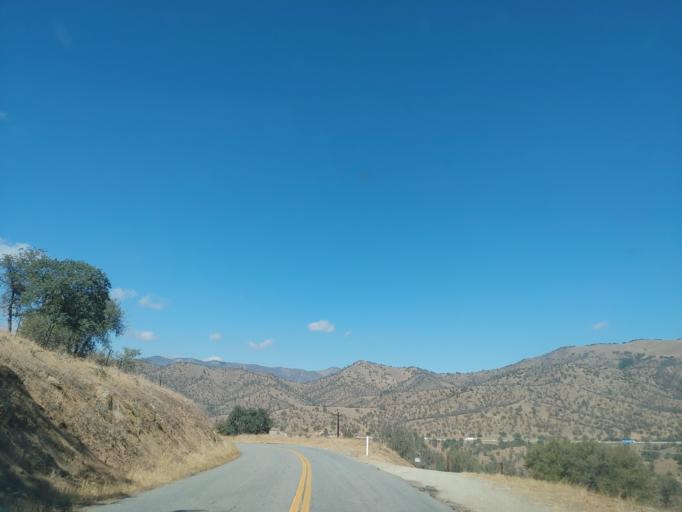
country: US
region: California
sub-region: Kern County
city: Golden Hills
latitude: 35.1847
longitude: -118.5167
